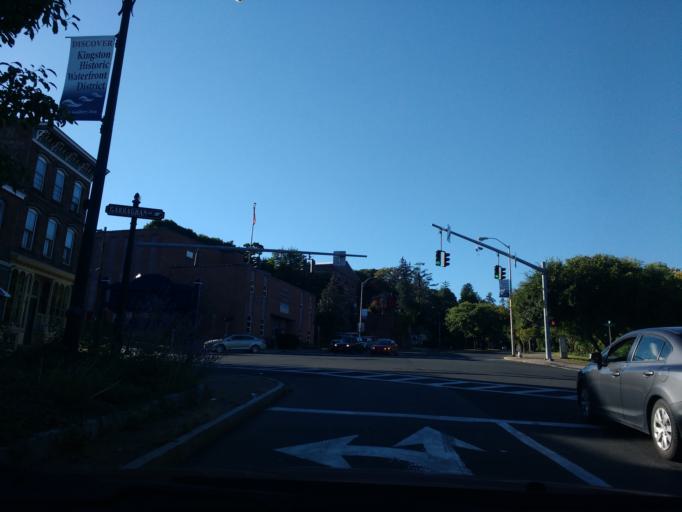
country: US
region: New York
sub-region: Ulster County
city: Kingston
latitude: 41.9200
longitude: -73.9856
